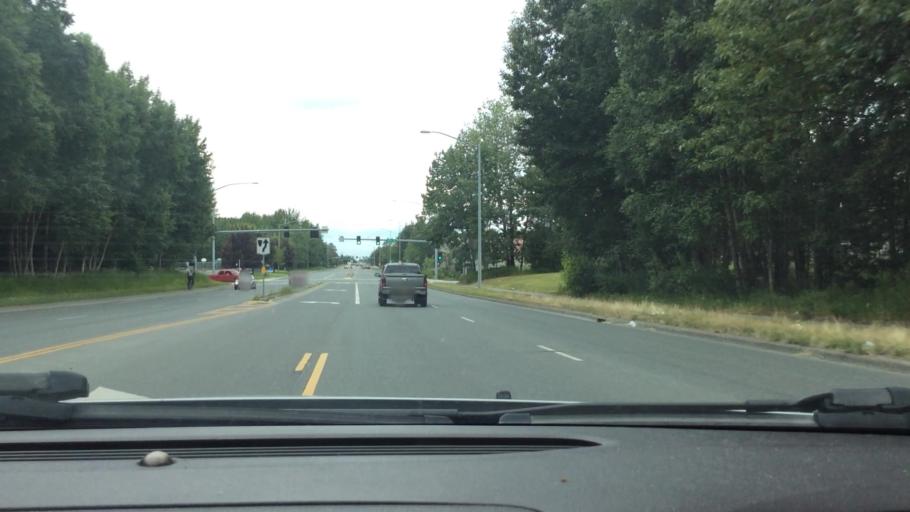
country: US
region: Alaska
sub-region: Anchorage Municipality
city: Anchorage
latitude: 61.2097
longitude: -149.7910
